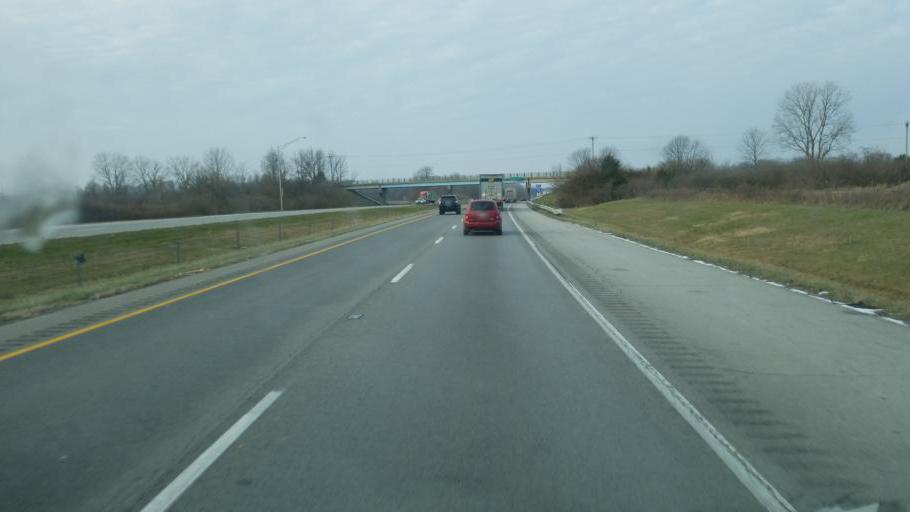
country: US
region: Indiana
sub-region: Morgan County
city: Mooresville
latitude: 39.6508
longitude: -86.4020
